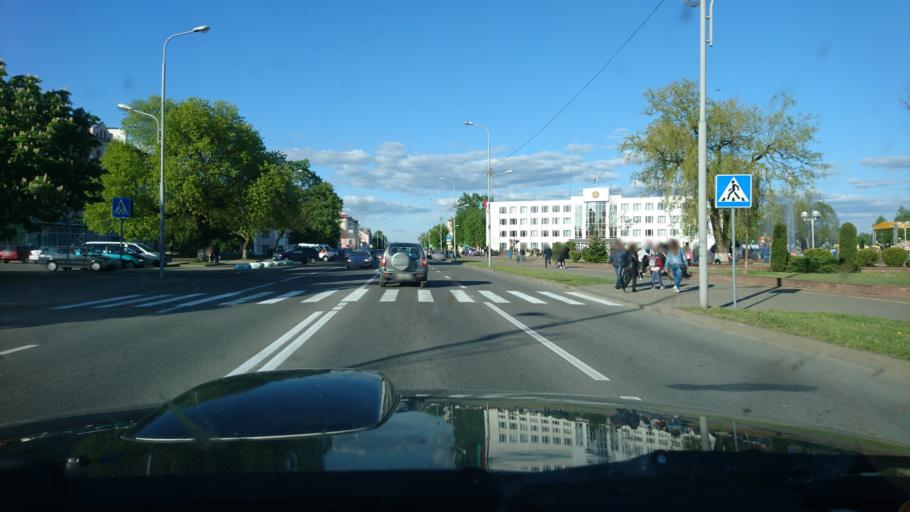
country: BY
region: Brest
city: Ivatsevichy
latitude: 52.7089
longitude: 25.3370
